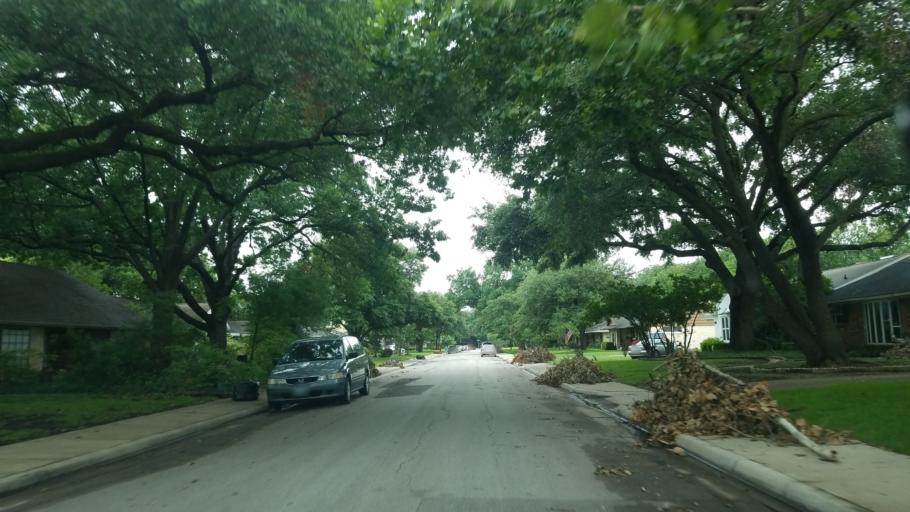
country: US
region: Texas
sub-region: Dallas County
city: Farmers Branch
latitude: 32.8932
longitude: -96.8668
